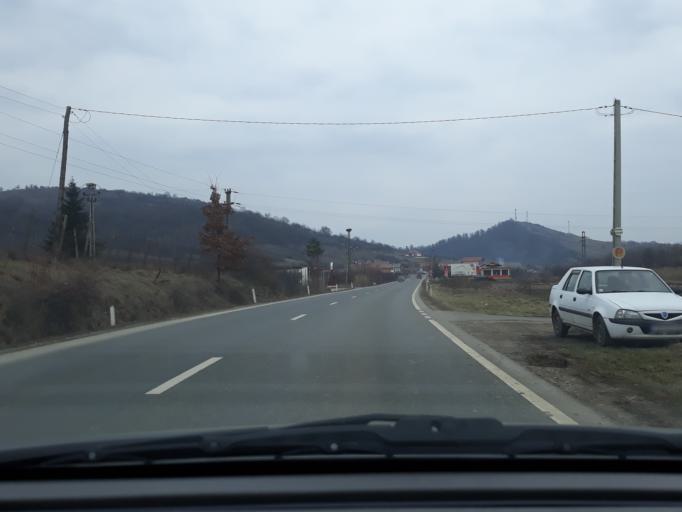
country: RO
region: Salaj
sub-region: Oras Simleu Silvaniei
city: Cehei
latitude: 47.2255
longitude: 22.7615
